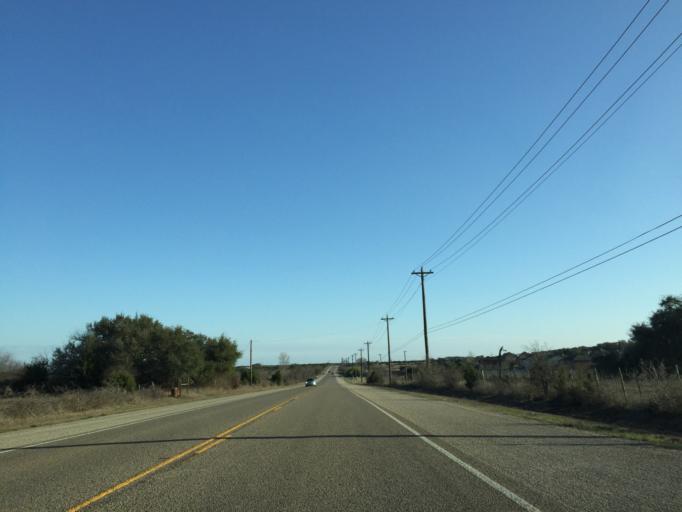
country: US
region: Texas
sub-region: Williamson County
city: Florence
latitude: 30.7567
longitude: -97.8089
